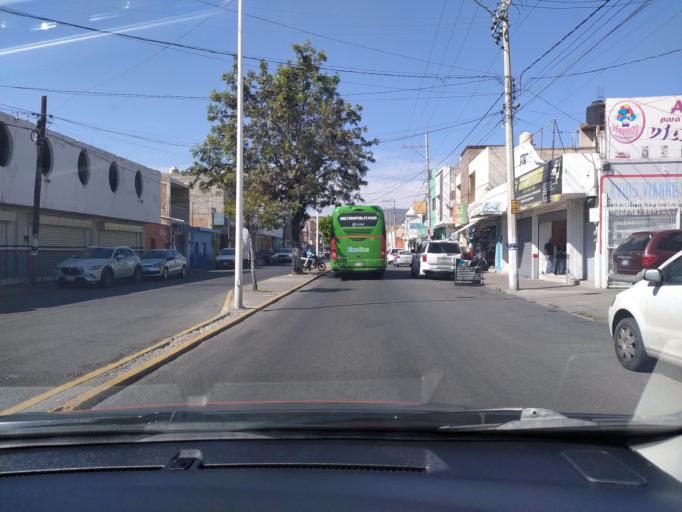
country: LA
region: Oudomxai
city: Muang La
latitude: 21.0159
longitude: 101.8554
